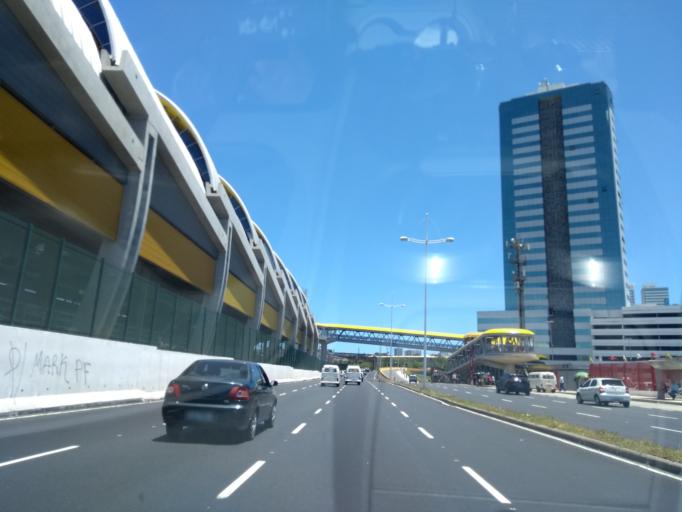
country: BR
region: Bahia
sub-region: Salvador
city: Salvador
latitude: -12.9758
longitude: -38.4583
